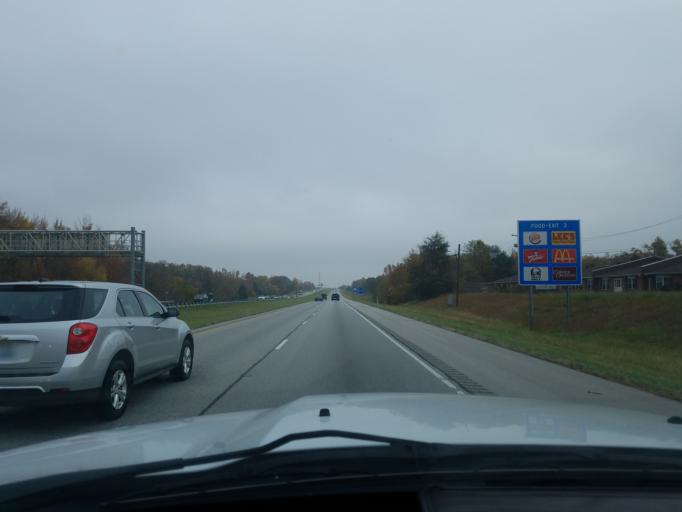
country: US
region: Indiana
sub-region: Floyd County
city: New Albany
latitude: 38.3249
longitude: -85.8359
